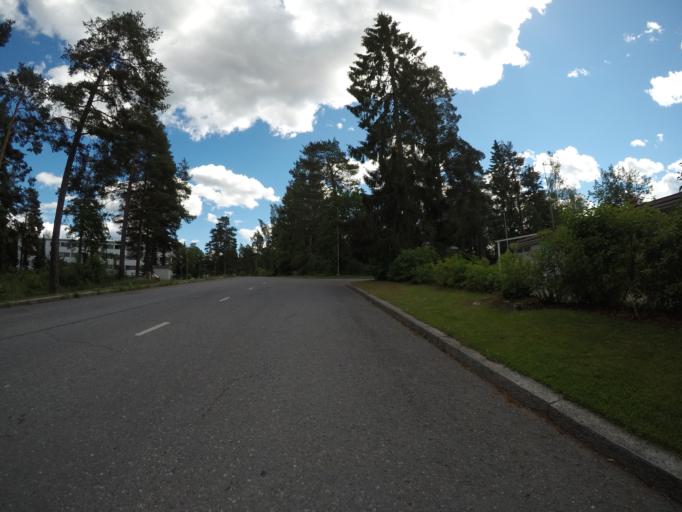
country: FI
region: Haeme
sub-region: Haemeenlinna
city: Haemeenlinna
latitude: 61.0162
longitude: 24.4329
